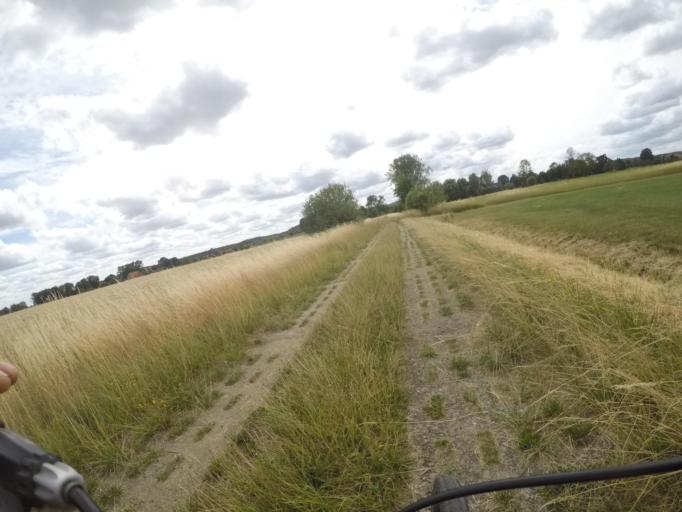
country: DE
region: Lower Saxony
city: Hitzacker
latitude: 53.1891
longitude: 11.0175
